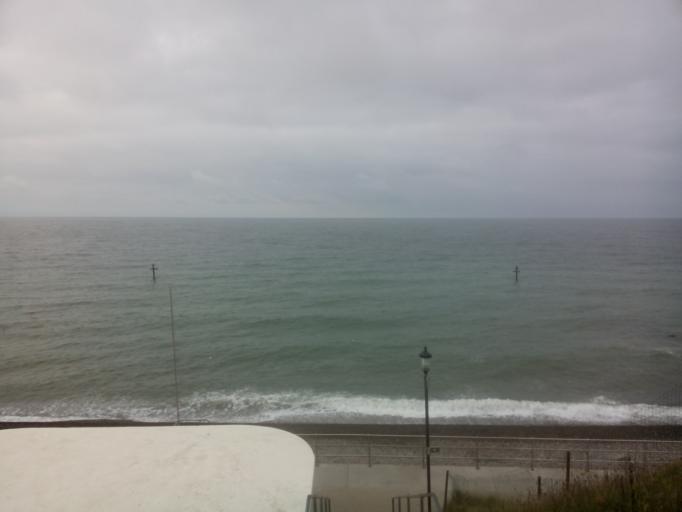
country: GB
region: England
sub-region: Norfolk
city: Sheringham
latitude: 52.9456
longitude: 1.2084
